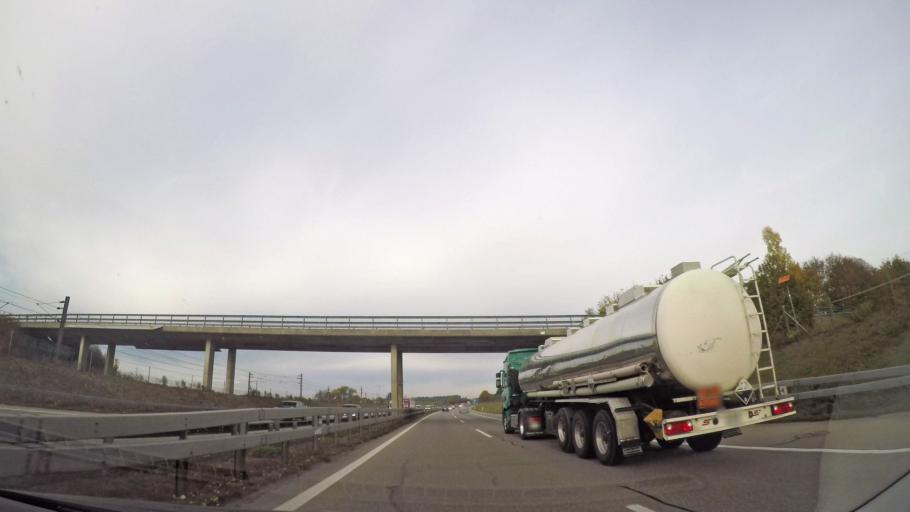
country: CH
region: Bern
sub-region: Emmental District
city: Hindelbank
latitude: 47.0531
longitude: 7.5391
